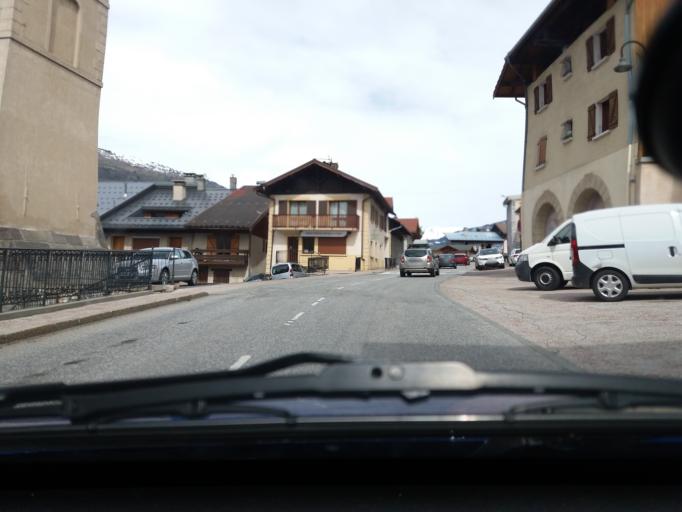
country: FR
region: Rhone-Alpes
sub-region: Departement de la Savoie
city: Macot-la-Plagne
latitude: 45.5537
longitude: 6.6726
